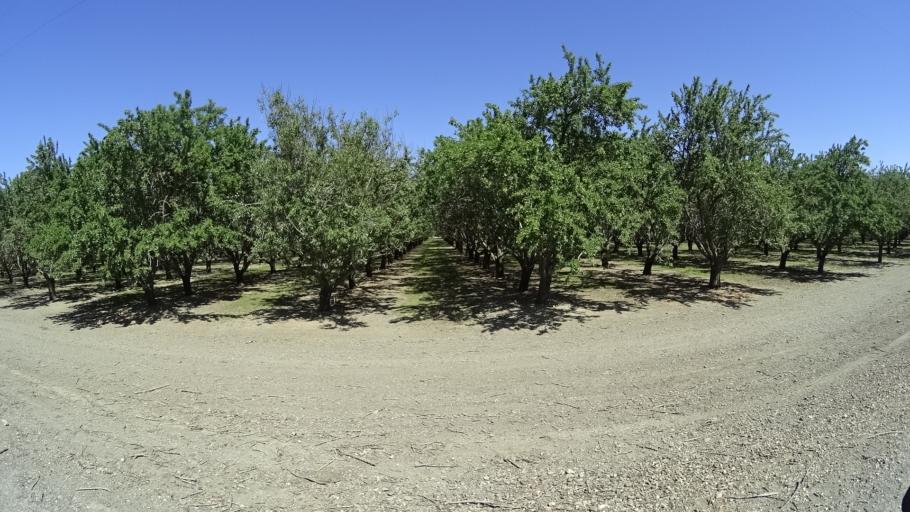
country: US
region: California
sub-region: Glenn County
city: Orland
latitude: 39.7215
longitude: -122.1337
